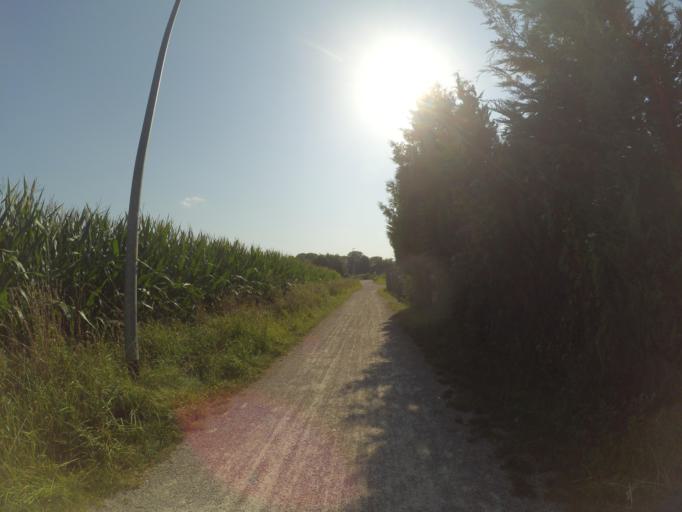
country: DE
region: Bavaria
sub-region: Swabia
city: Buchloe
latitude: 48.0424
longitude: 10.7238
